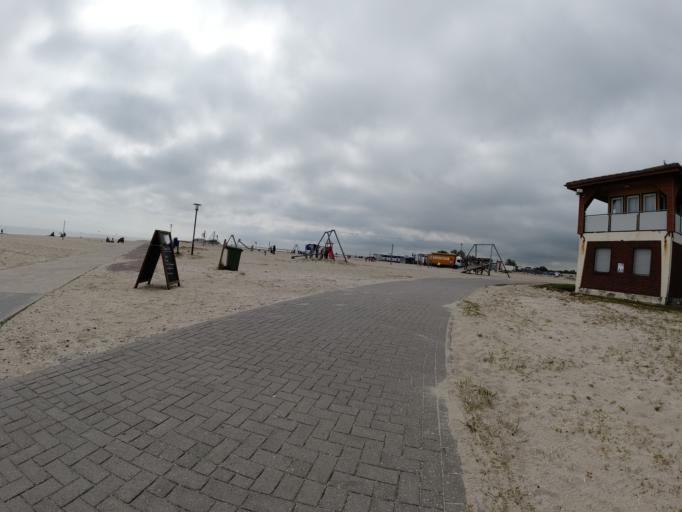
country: DE
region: Lower Saxony
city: Schillig
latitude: 53.7014
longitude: 8.0298
